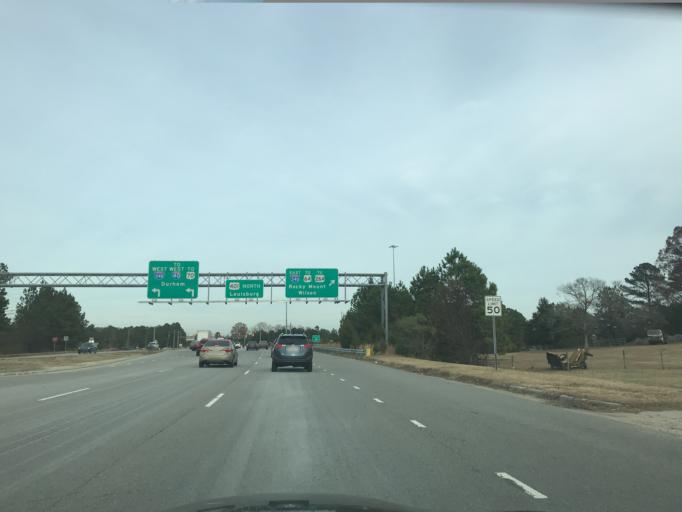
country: US
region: North Carolina
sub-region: Wake County
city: Knightdale
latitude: 35.8600
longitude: -78.5503
